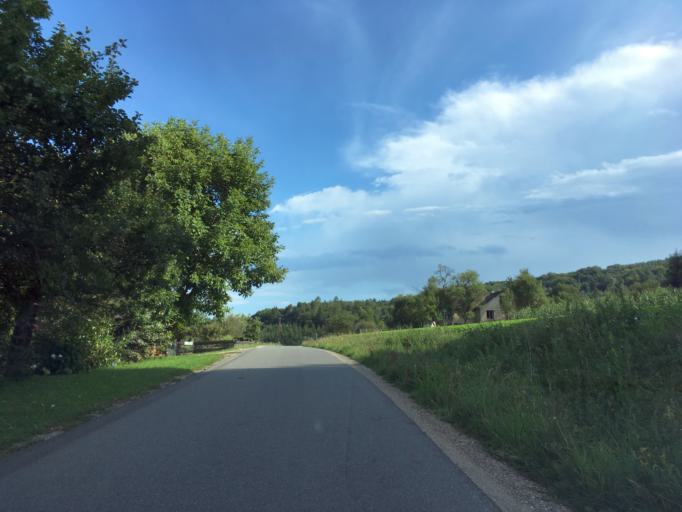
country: AT
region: Styria
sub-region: Politischer Bezirk Leibnitz
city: Sankt Nikolai im Sausal
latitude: 46.8119
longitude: 15.4549
